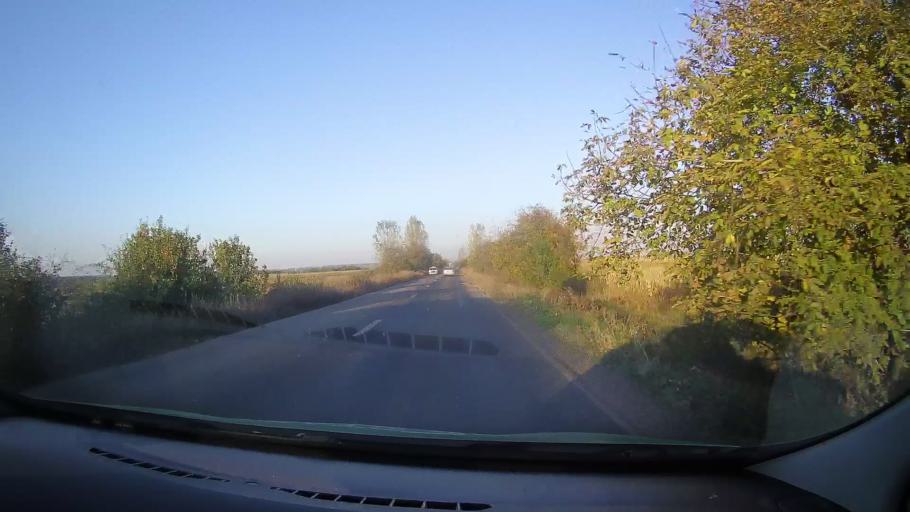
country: RO
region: Bihor
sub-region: Comuna Salard
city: Salard
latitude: 47.1986
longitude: 22.0054
